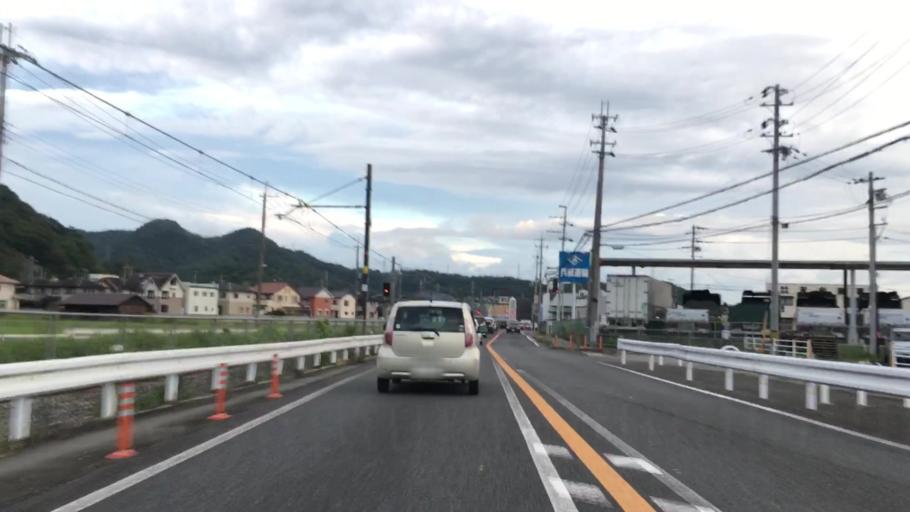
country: JP
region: Hyogo
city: Himeji
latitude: 34.8785
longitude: 134.7290
